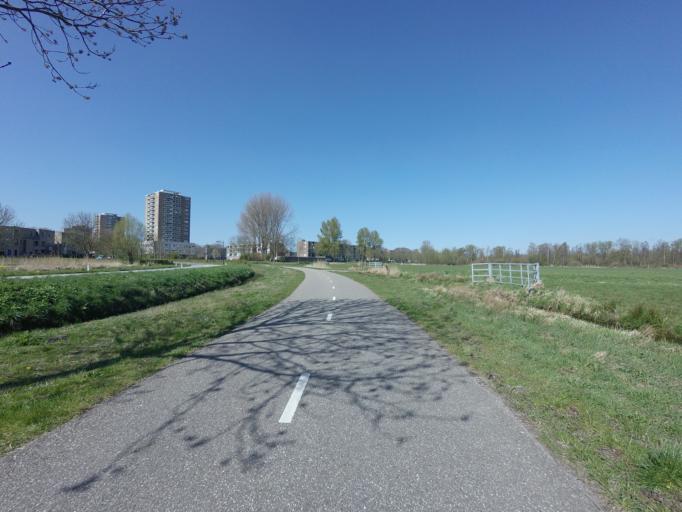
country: NL
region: North Holland
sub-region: Gemeente Haarlem
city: Haarlem
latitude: 52.3602
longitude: 4.6691
